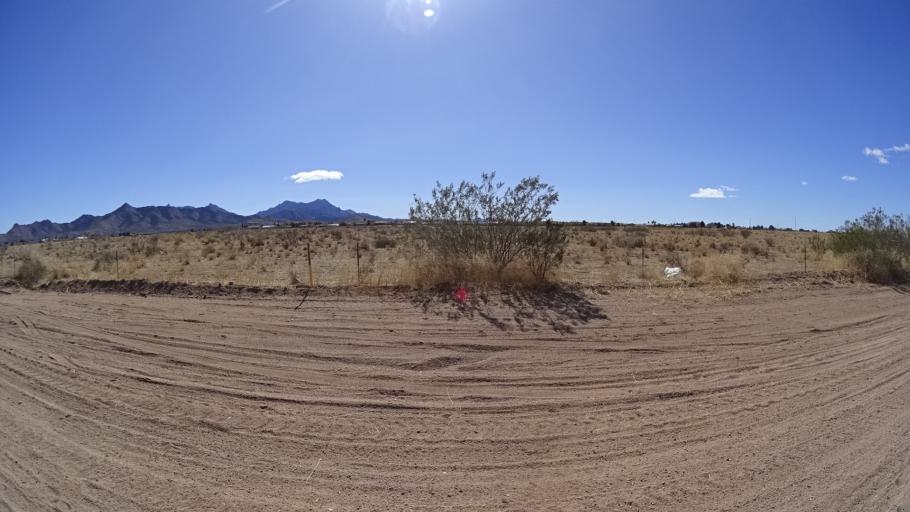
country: US
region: Arizona
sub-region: Mohave County
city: Kingman
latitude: 35.2010
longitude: -113.9833
